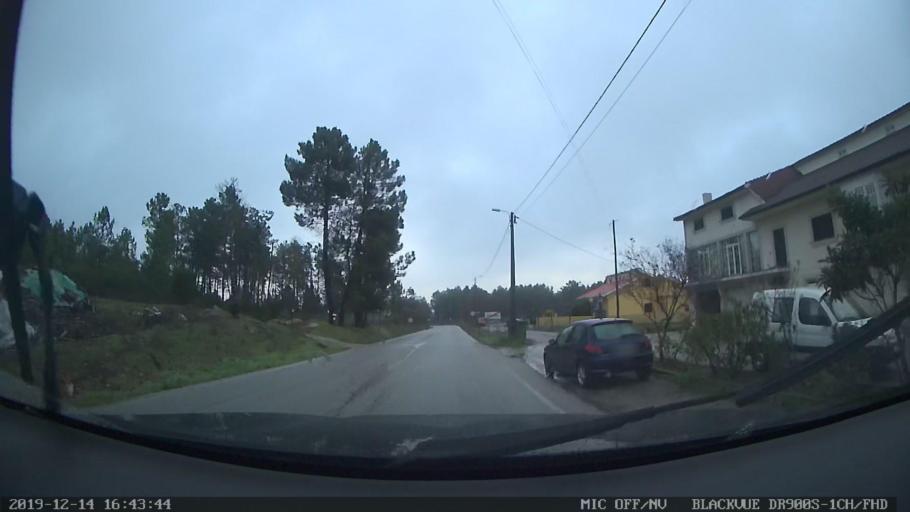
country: PT
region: Vila Real
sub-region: Murca
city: Murca
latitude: 41.3849
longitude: -7.4990
